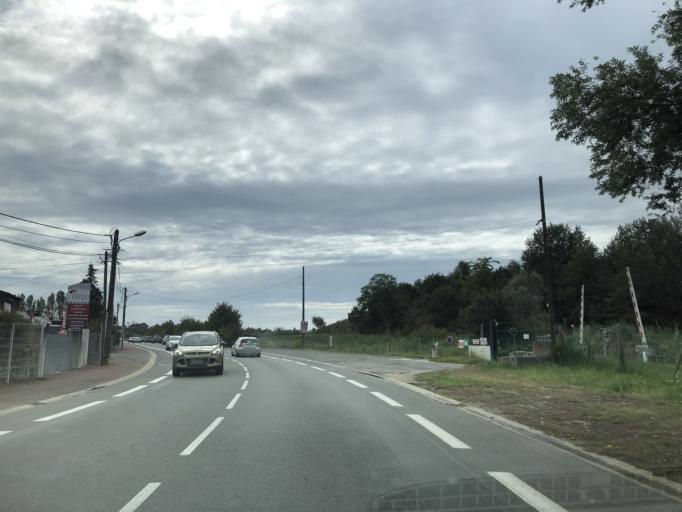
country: FR
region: Poitou-Charentes
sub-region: Departement de la Charente-Maritime
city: Royan
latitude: 45.6318
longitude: -1.0027
